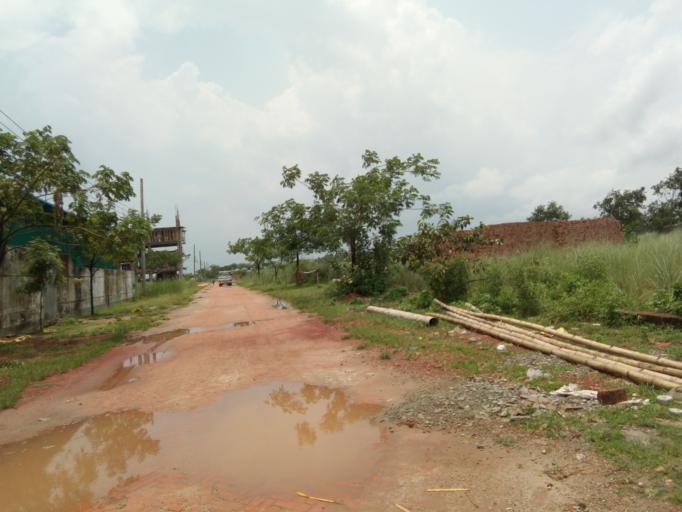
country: BD
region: Dhaka
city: Azimpur
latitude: 23.7519
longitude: 90.3383
